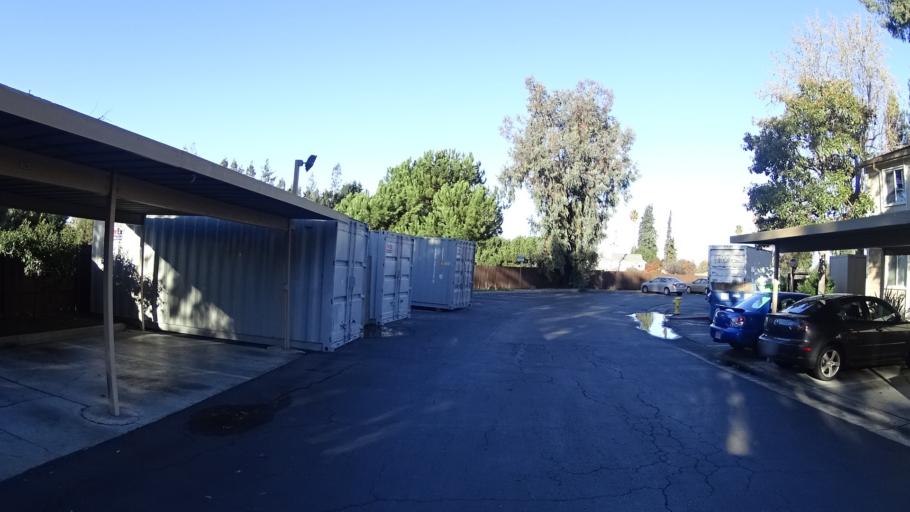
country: US
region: California
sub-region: Santa Clara County
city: Sunnyvale
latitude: 37.3831
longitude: -122.0300
